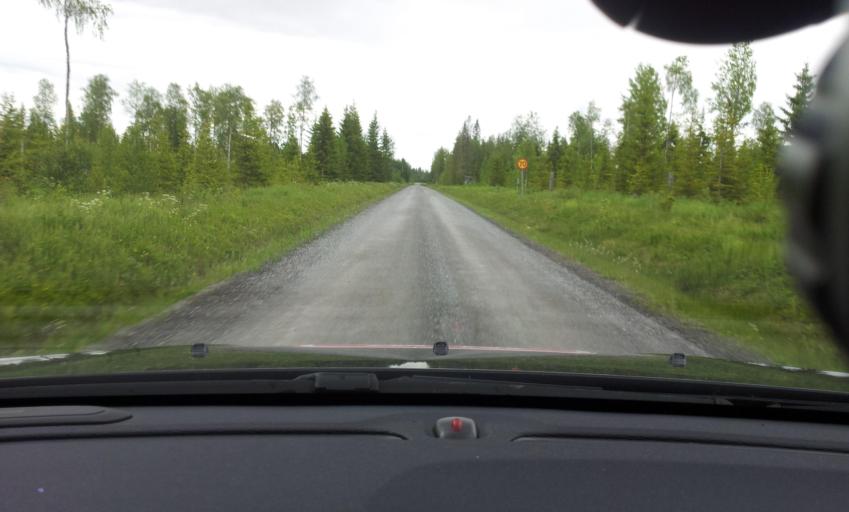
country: SE
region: Jaemtland
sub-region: OEstersunds Kommun
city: Brunflo
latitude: 63.1437
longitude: 15.0503
